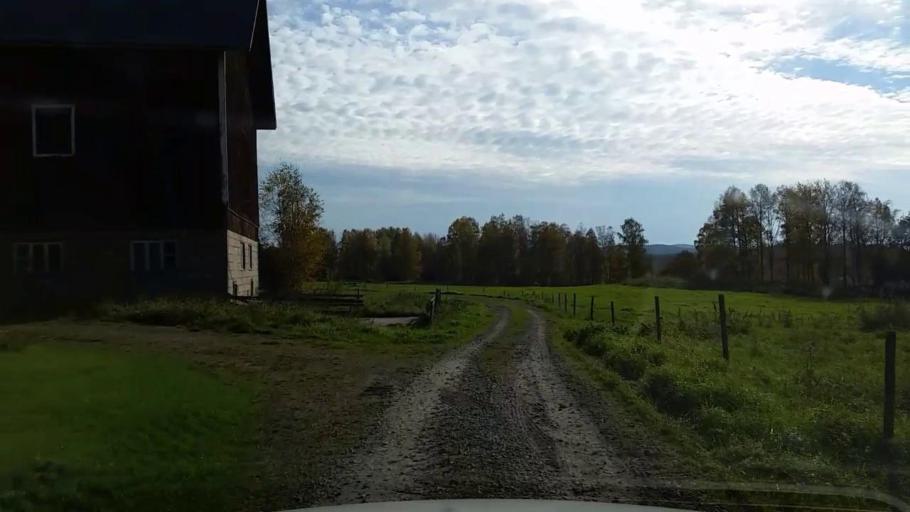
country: SE
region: Gaevleborg
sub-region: Ljusdals Kommun
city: Jaervsoe
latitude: 61.7836
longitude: 16.1659
